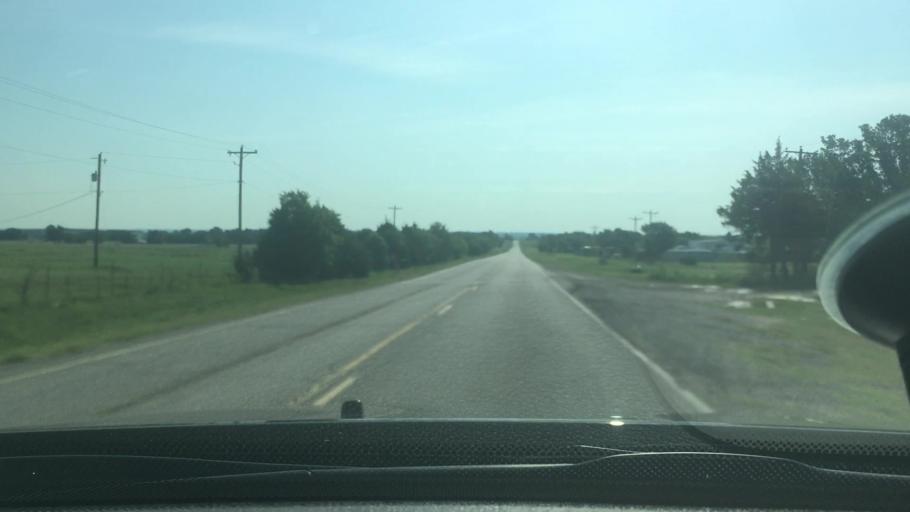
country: US
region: Oklahoma
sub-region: Garvin County
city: Wynnewood
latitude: 34.6517
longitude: -97.2417
